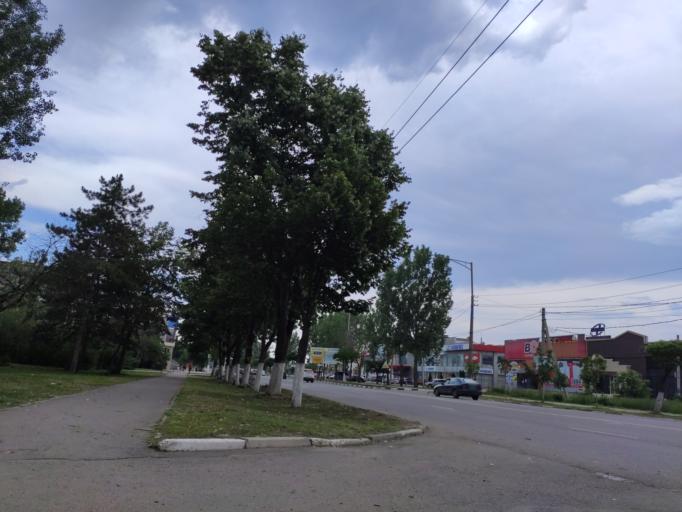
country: MD
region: Balti
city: Balti
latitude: 47.7621
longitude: 27.9409
